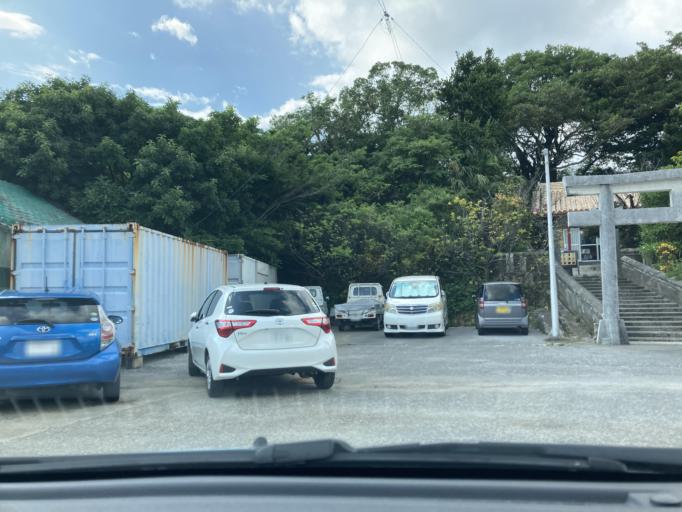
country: JP
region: Okinawa
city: Itoman
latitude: 26.1306
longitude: 127.7729
